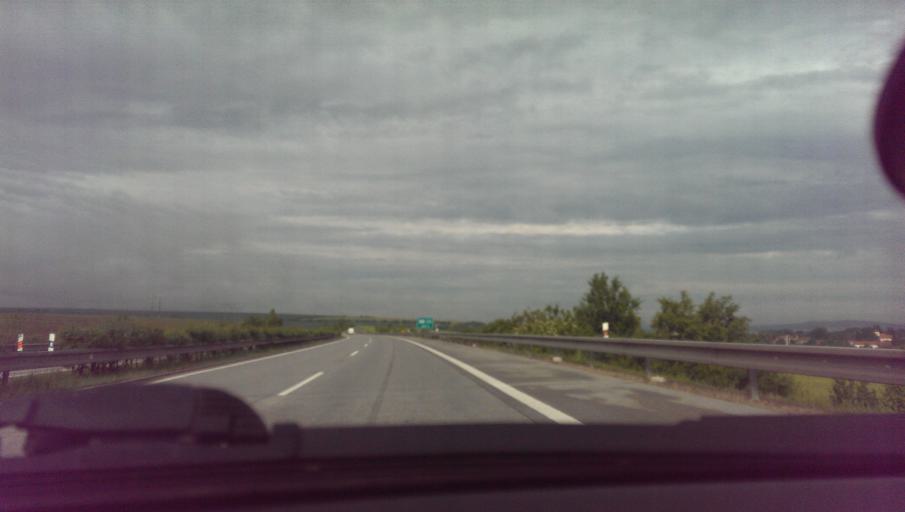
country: CZ
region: South Moravian
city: Ivanovice na Hane
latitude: 49.2780
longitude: 17.0553
